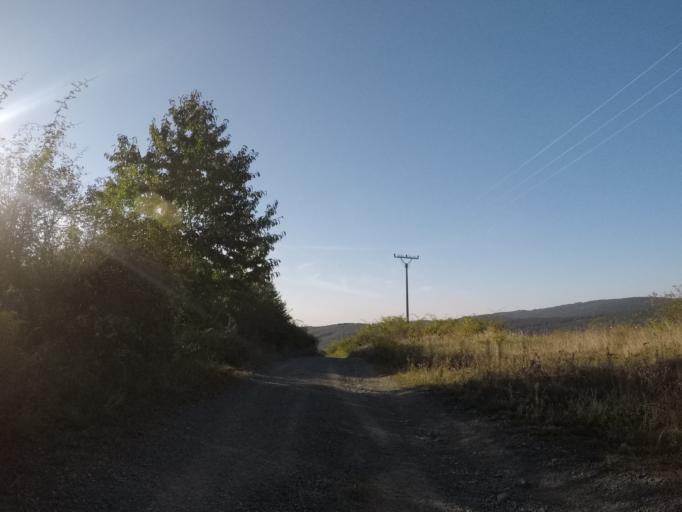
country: SK
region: Kosicky
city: Kosice
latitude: 48.7363
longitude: 21.1376
